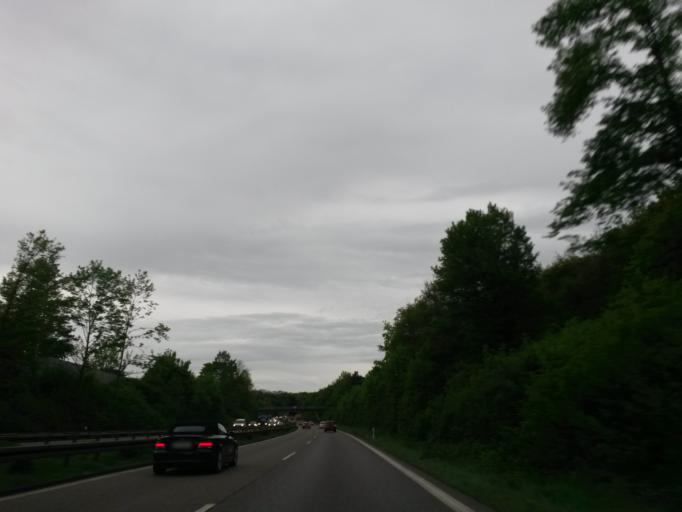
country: DE
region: Baden-Wuerttemberg
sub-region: Regierungsbezirk Stuttgart
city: Korntal
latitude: 48.8406
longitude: 9.1509
